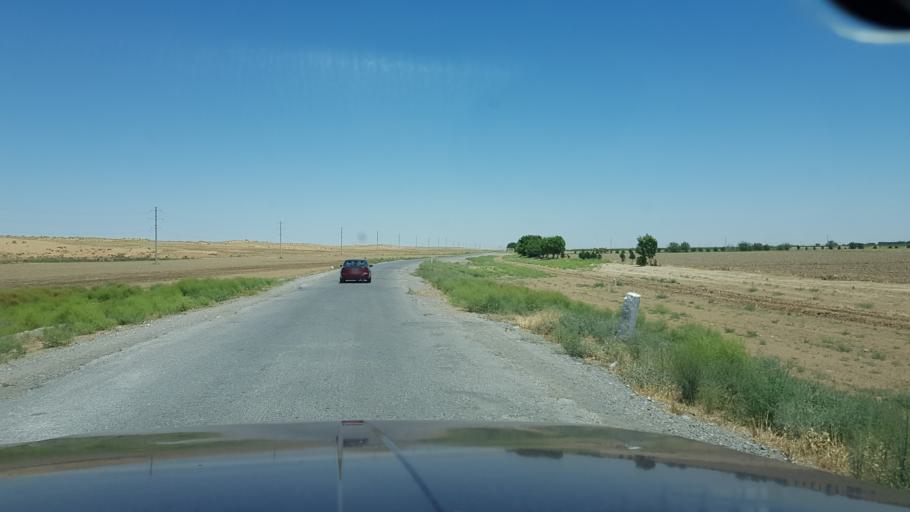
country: TM
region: Ahal
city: Annau
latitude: 37.8582
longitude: 58.7077
